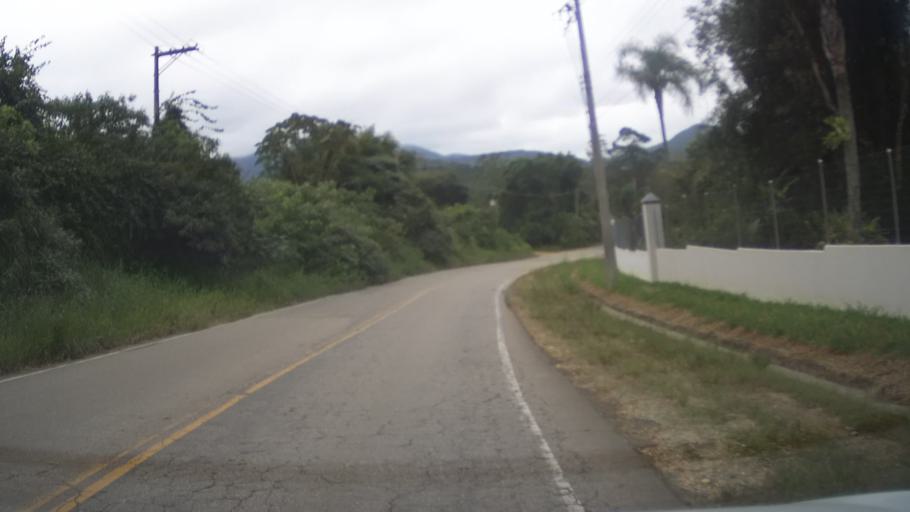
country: BR
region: Sao Paulo
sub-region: Aruja
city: Aruja
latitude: -23.3418
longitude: -46.4046
